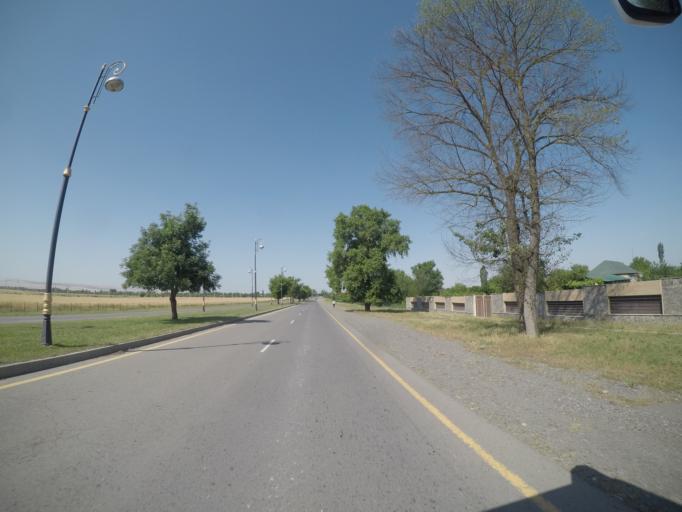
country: AZ
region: Qabala Rayon
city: Qutqashen
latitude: 40.8518
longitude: 47.7437
